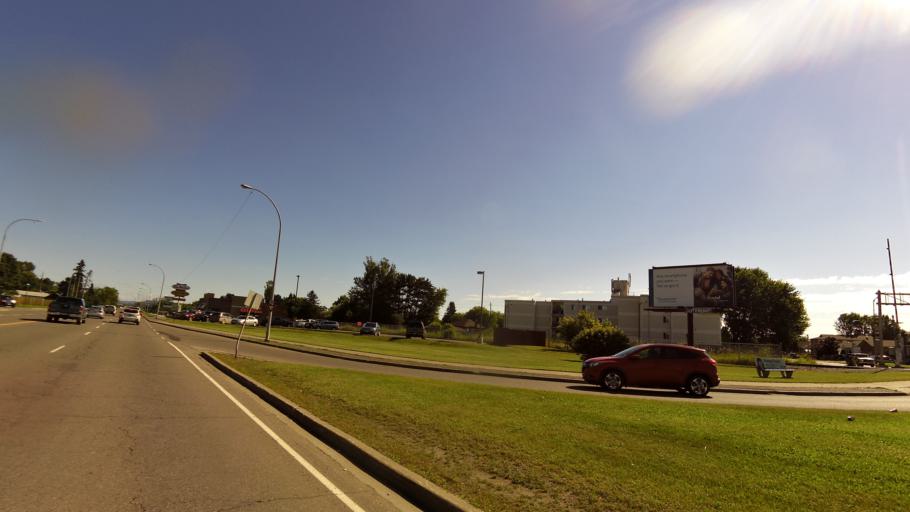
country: CA
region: Ontario
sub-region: Thunder Bay District
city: Thunder Bay
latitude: 48.3843
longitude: -89.2626
